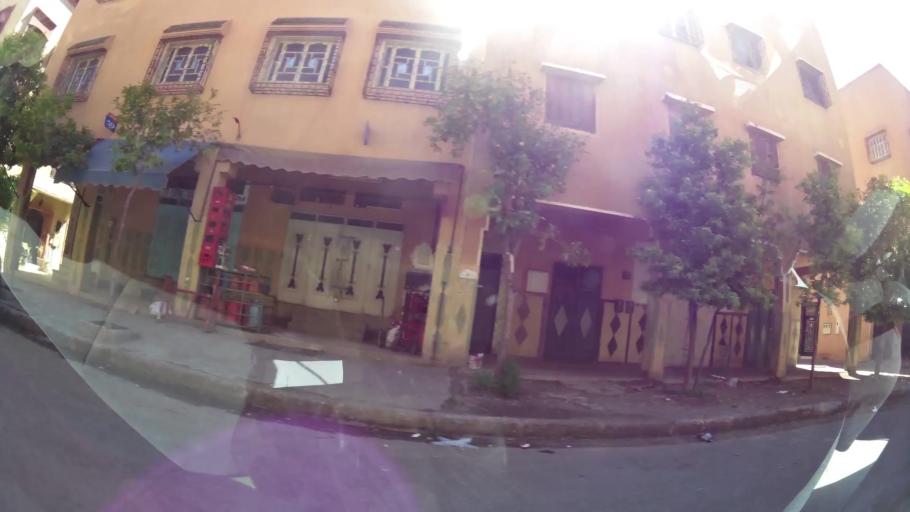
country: MA
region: Marrakech-Tensift-Al Haouz
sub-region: Marrakech
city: Marrakesh
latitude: 31.6351
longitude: -8.0696
